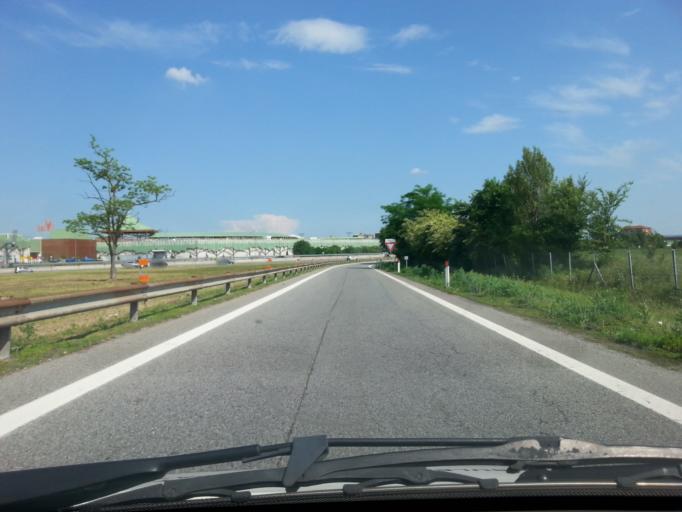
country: IT
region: Piedmont
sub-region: Provincia di Torino
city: Nichelino
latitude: 45.0060
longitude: 7.6190
